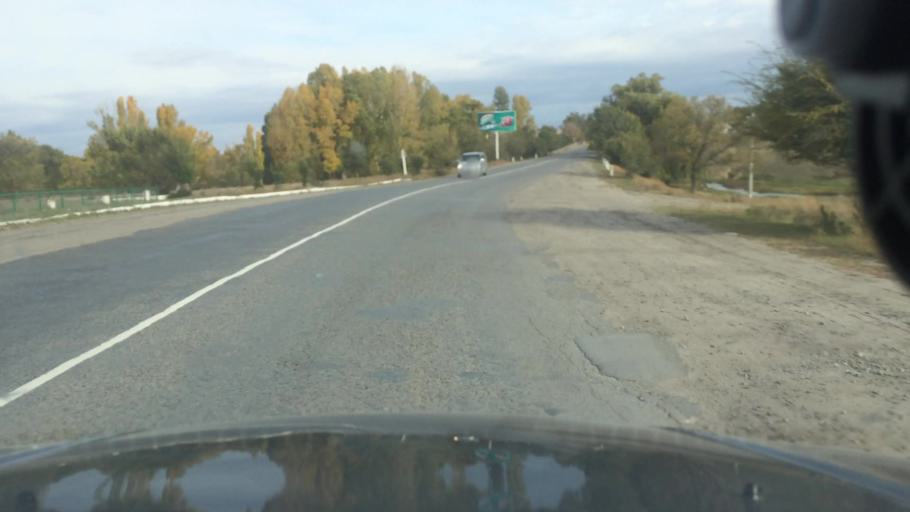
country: KG
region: Ysyk-Koel
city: Karakol
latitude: 42.5325
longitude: 78.3816
